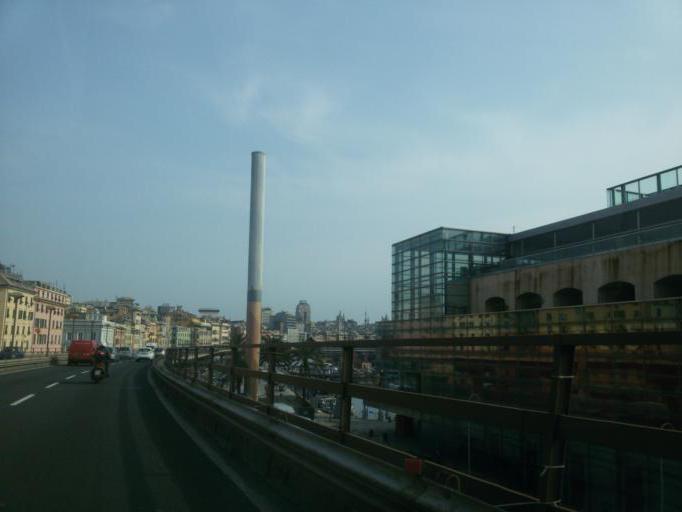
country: IT
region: Liguria
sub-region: Provincia di Genova
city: San Teodoro
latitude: 44.4149
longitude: 8.9231
